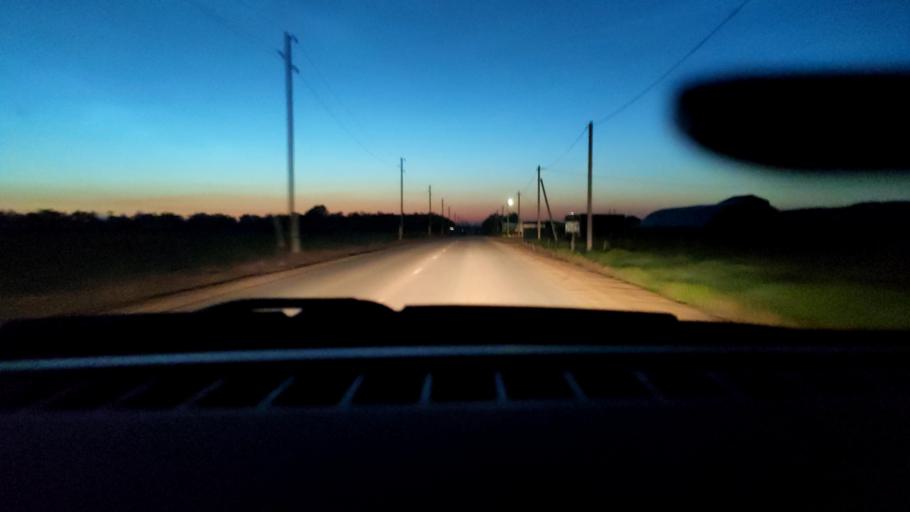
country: RU
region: Perm
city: Kultayevo
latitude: 57.8776
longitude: 55.9877
